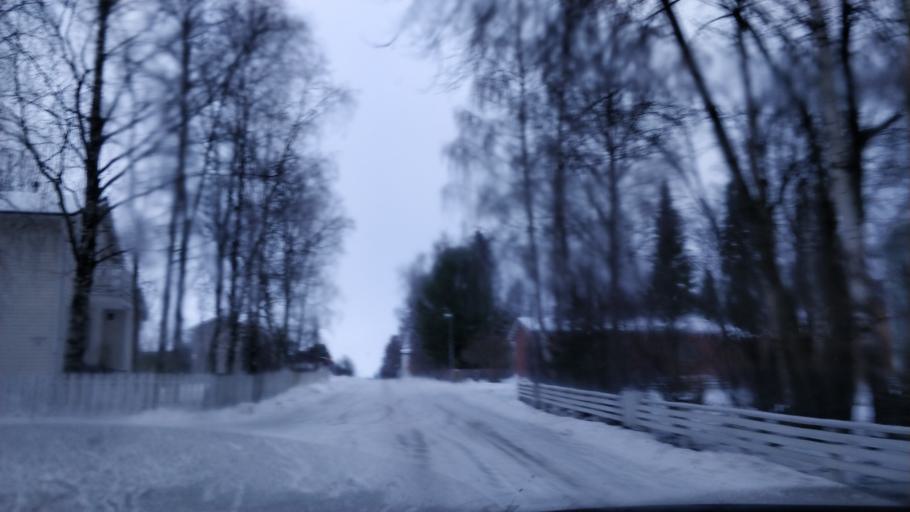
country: FI
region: Lapland
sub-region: Kemi-Tornio
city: Kemi
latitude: 65.7424
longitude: 24.5630
